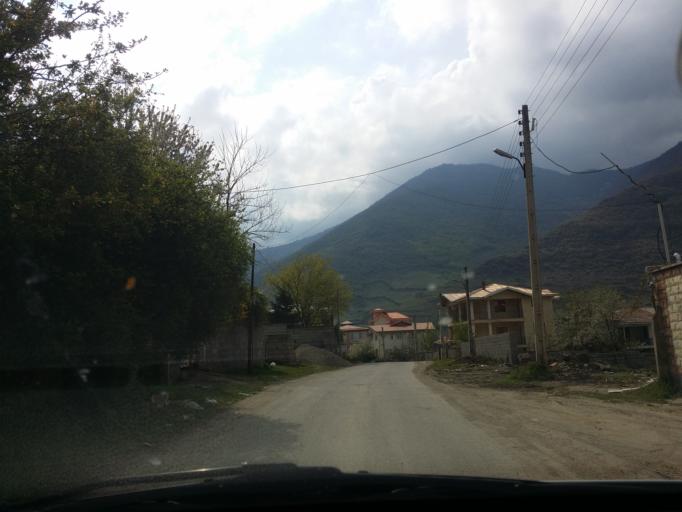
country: IR
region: Mazandaran
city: `Abbasabad
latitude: 36.4855
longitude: 51.1370
